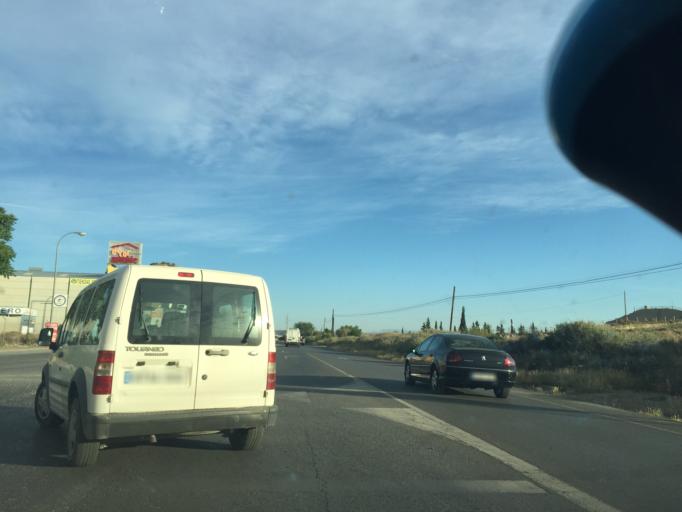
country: ES
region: Andalusia
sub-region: Provincia de Granada
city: Guadix
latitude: 37.3133
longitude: -3.1517
